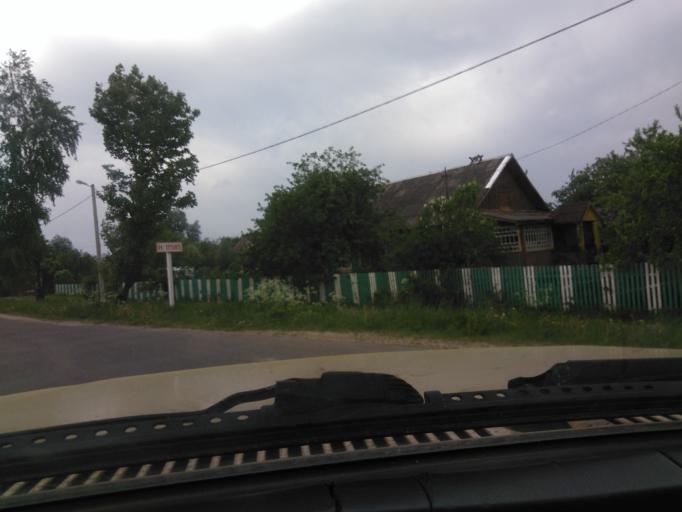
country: BY
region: Mogilev
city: Kamyennyya Lavy
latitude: 54.0548
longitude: 30.3264
